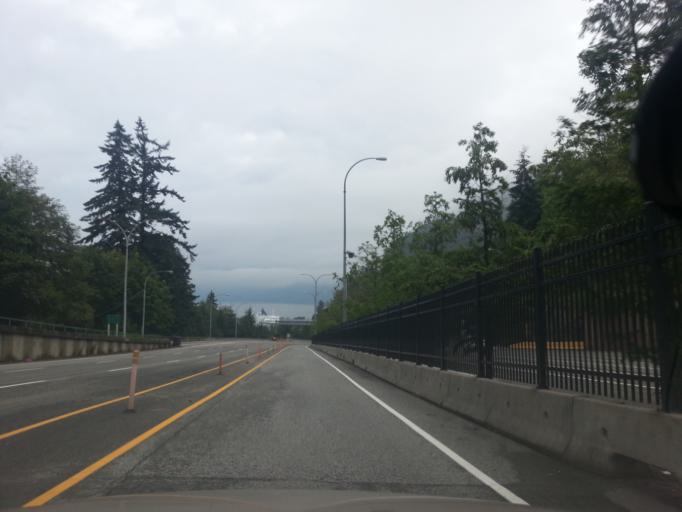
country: CA
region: British Columbia
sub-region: Greater Vancouver Regional District
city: Bowen Island
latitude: 49.3698
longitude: -123.2753
